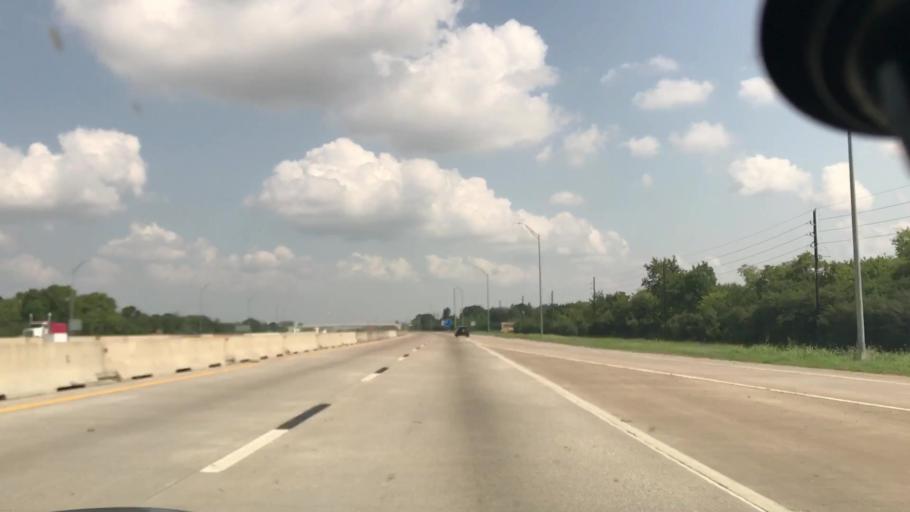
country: US
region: Texas
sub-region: Brazoria County
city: Iowa Colony
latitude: 29.5165
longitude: -95.3867
